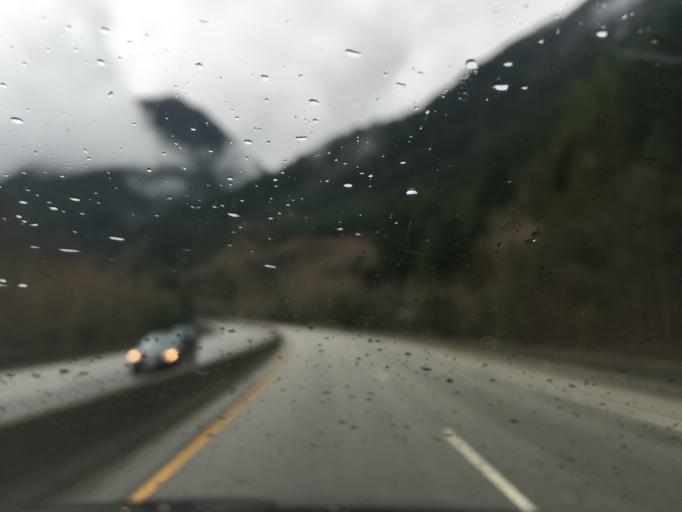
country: CA
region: British Columbia
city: Hope
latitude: 49.4396
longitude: -121.2995
